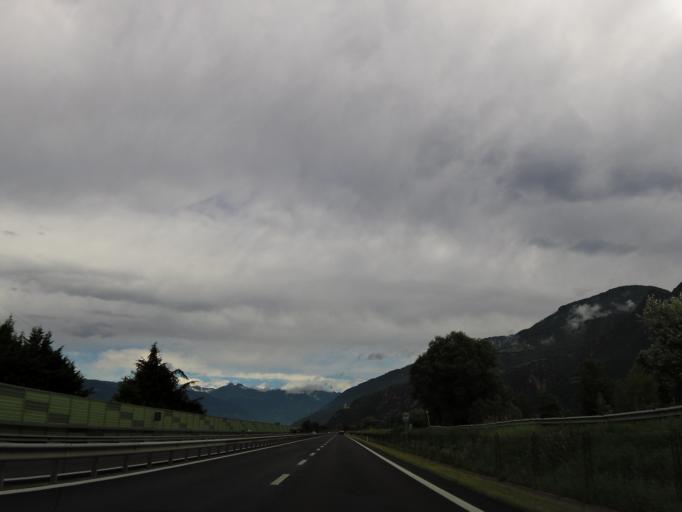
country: IT
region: Trentino-Alto Adige
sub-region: Bolzano
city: San Paolo
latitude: 46.5009
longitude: 11.2678
